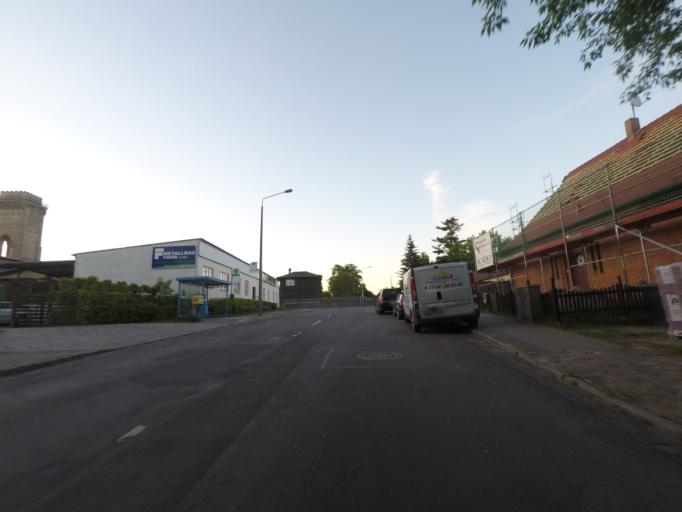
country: DE
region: Brandenburg
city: Melchow
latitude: 52.8459
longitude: 13.7259
